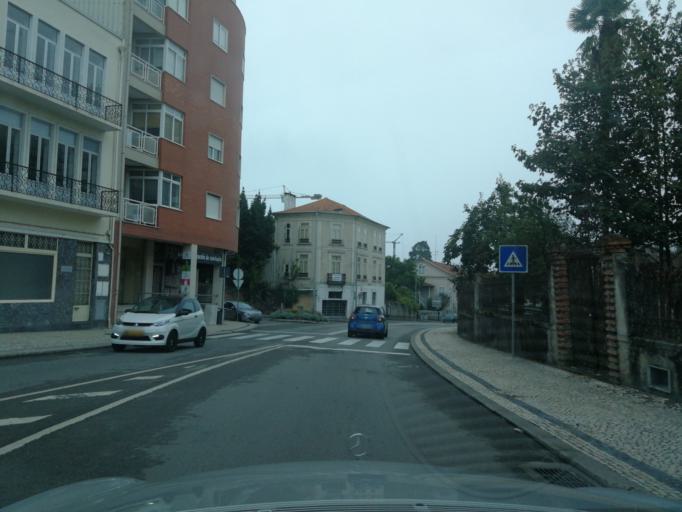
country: PT
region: Aveiro
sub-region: Agueda
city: Agueda
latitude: 40.5750
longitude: -8.4482
